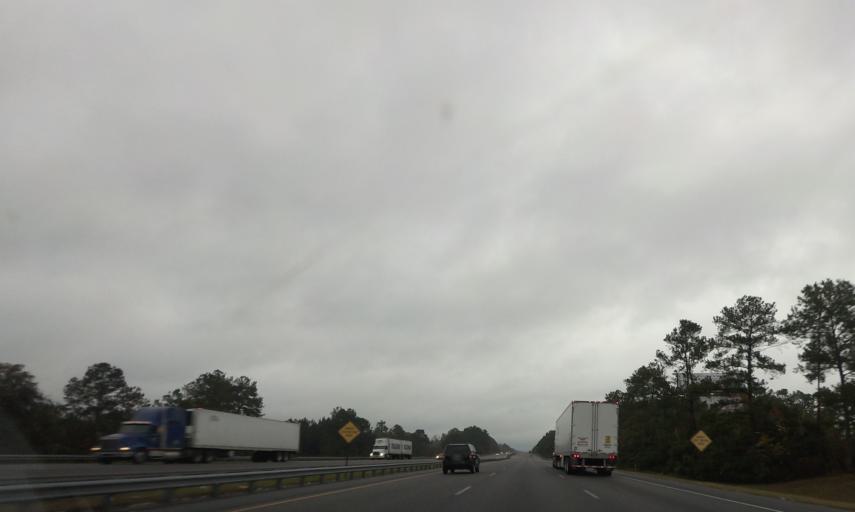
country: US
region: Georgia
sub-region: Lowndes County
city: Valdosta
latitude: 30.7044
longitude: -83.2468
